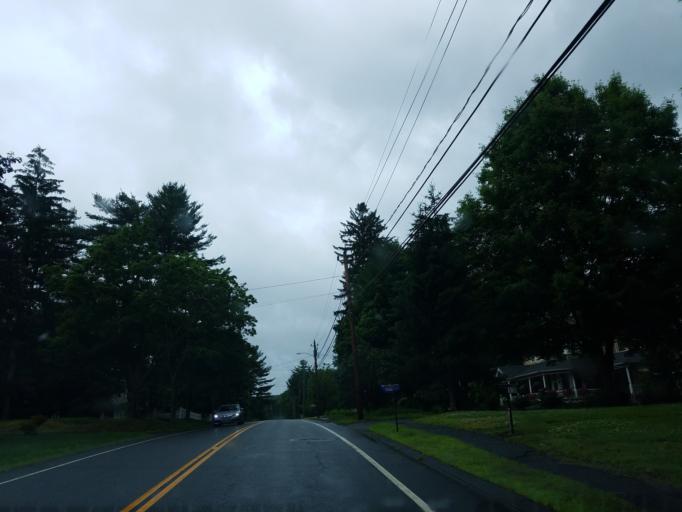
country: US
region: Connecticut
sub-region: Hartford County
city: Collinsville
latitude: 41.7637
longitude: -72.8891
